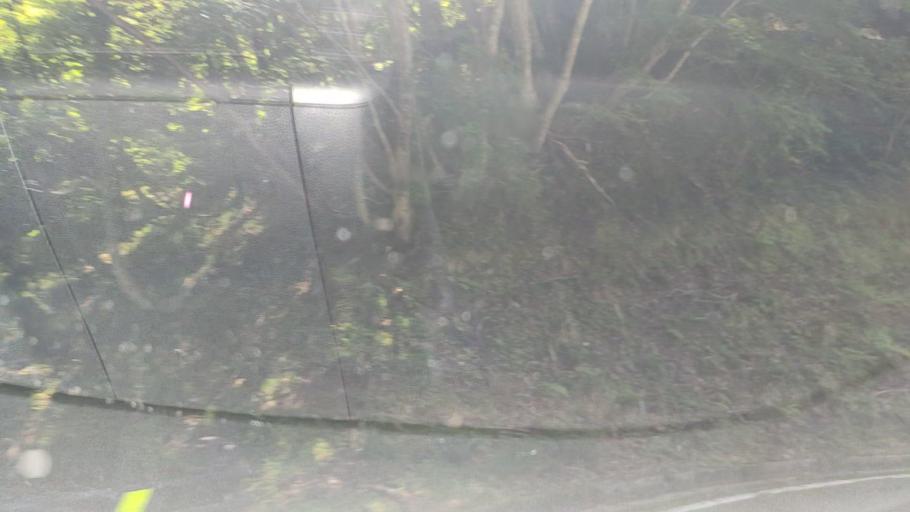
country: JP
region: Tottori
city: Tottori
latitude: 35.3727
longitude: 134.4922
